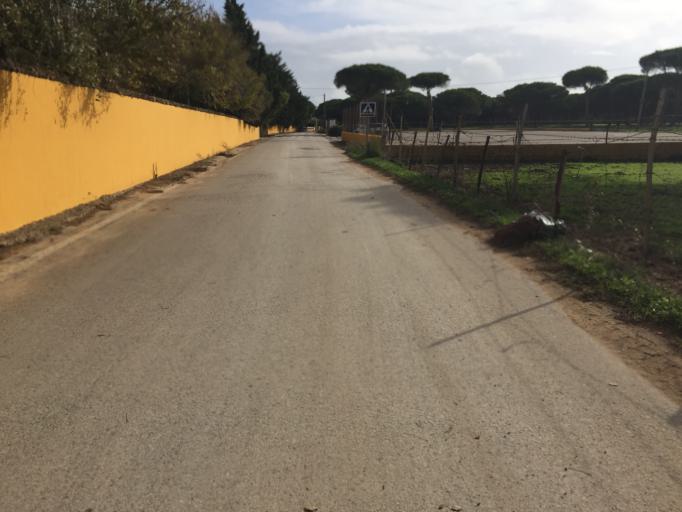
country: ES
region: Andalusia
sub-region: Provincia de Cadiz
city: Conil de la Frontera
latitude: 36.3108
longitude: -6.1137
